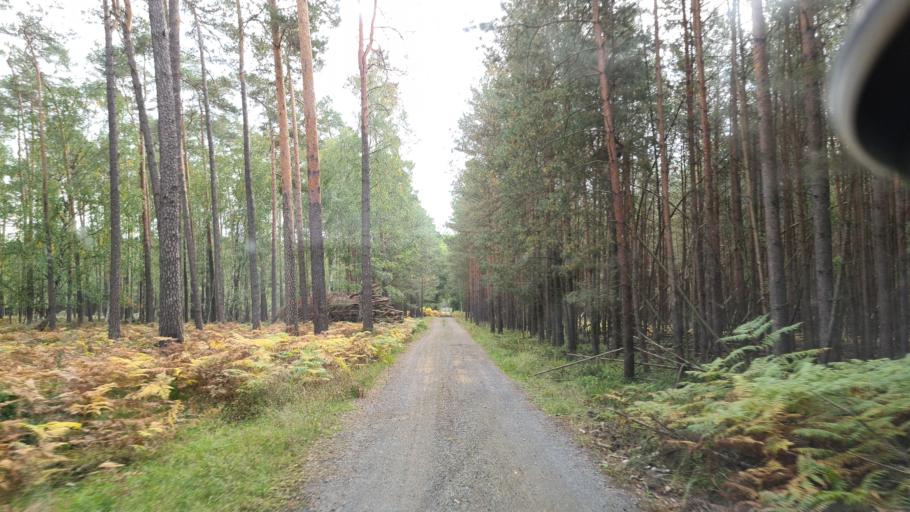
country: DE
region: Brandenburg
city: Schonewalde
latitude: 51.7191
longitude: 13.5751
